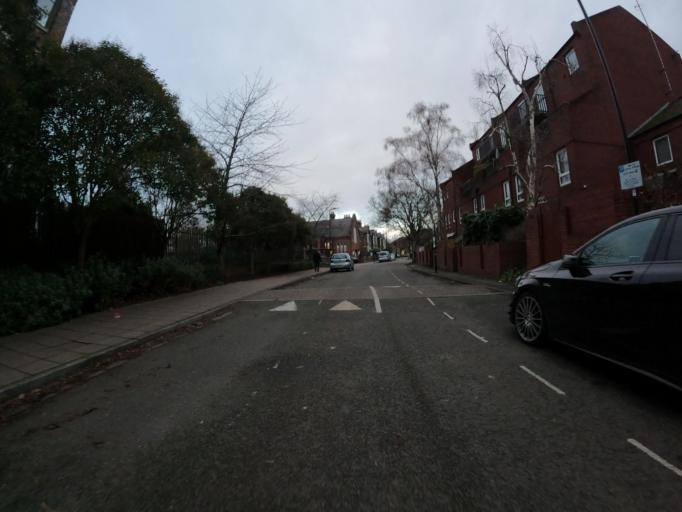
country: GB
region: England
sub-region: Greater London
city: Acton
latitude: 51.4971
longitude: -0.2654
